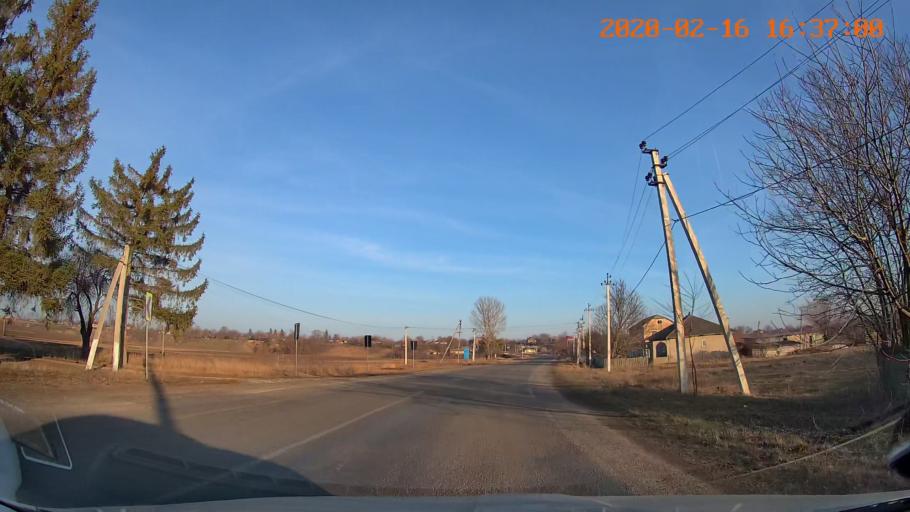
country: RO
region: Botosani
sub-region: Comuna Paltinis
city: Paltinis
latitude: 48.2708
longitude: 26.7017
